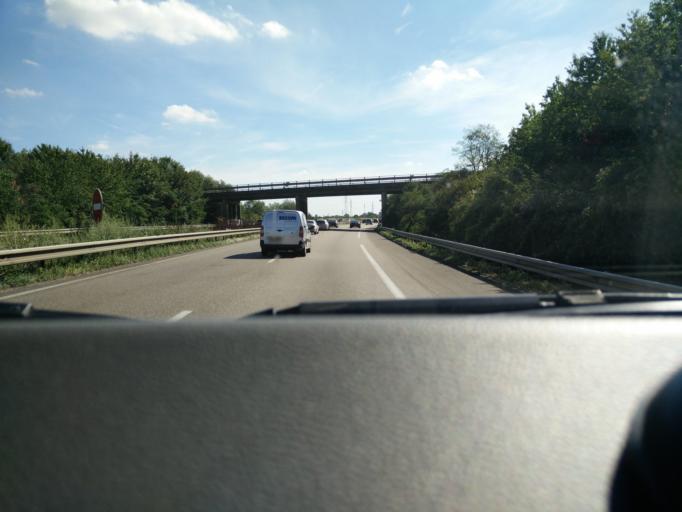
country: FR
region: Lorraine
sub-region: Departement de la Moselle
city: Bertrange
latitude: 49.3013
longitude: 6.1840
